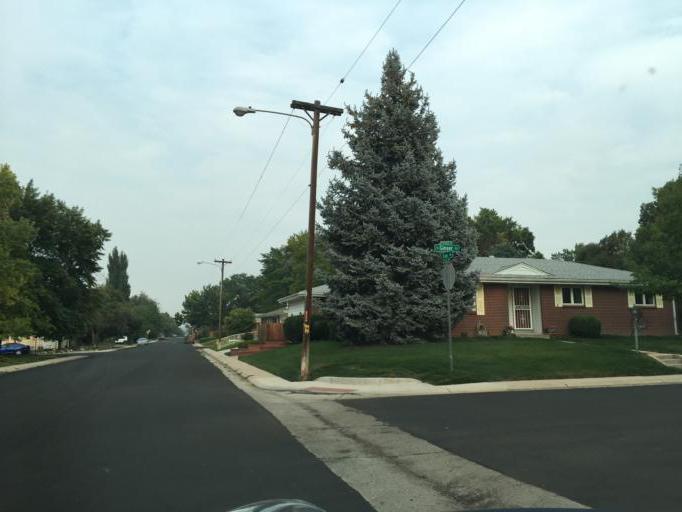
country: US
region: Colorado
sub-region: Arapahoe County
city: Glendale
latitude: 39.6876
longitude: -104.9255
